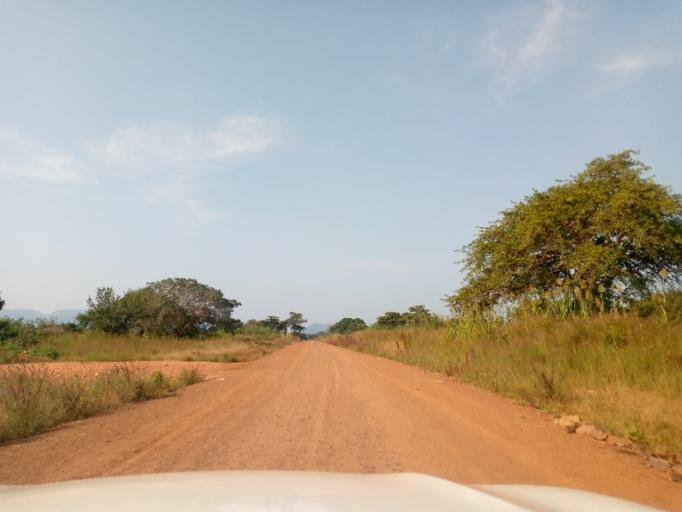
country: ET
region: Oromiya
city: Mendi
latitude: 10.1431
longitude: 34.9500
